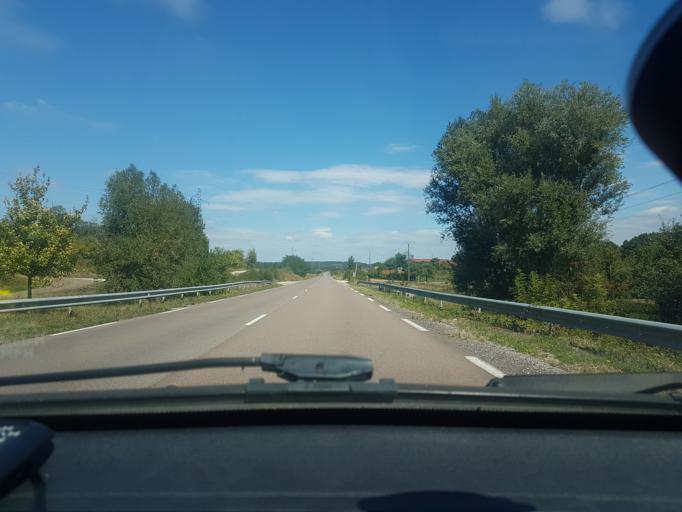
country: FR
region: Franche-Comte
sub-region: Departement de la Haute-Saone
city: Gray-la-Ville
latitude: 47.4205
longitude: 5.5220
